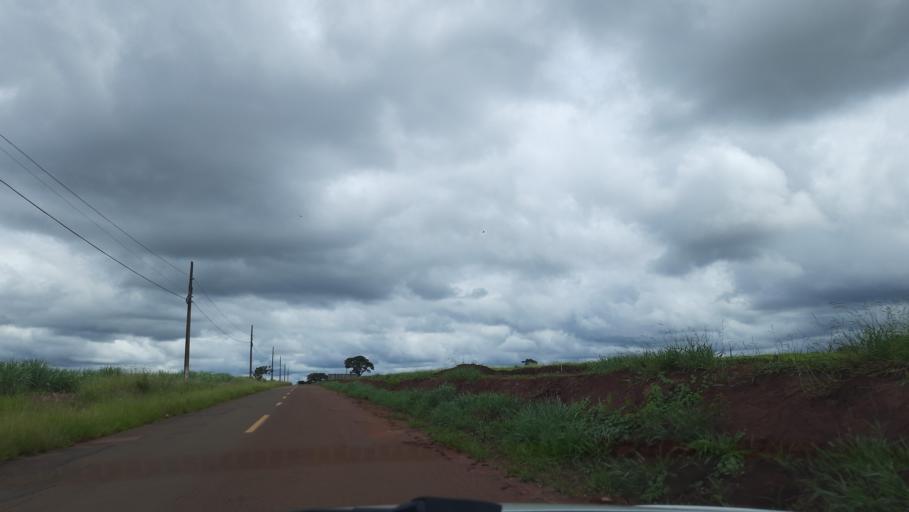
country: BR
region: Sao Paulo
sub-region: Casa Branca
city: Casa Branca
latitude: -21.7948
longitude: -47.0980
